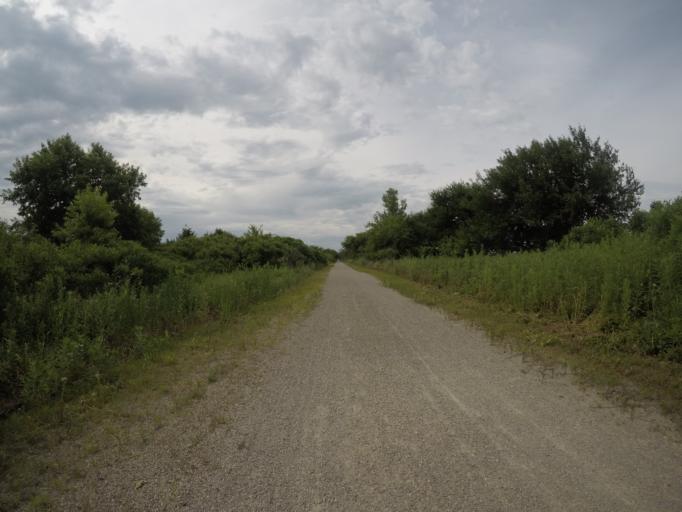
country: US
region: Kansas
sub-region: Anderson County
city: Garnett
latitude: 38.4322
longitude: -95.2637
